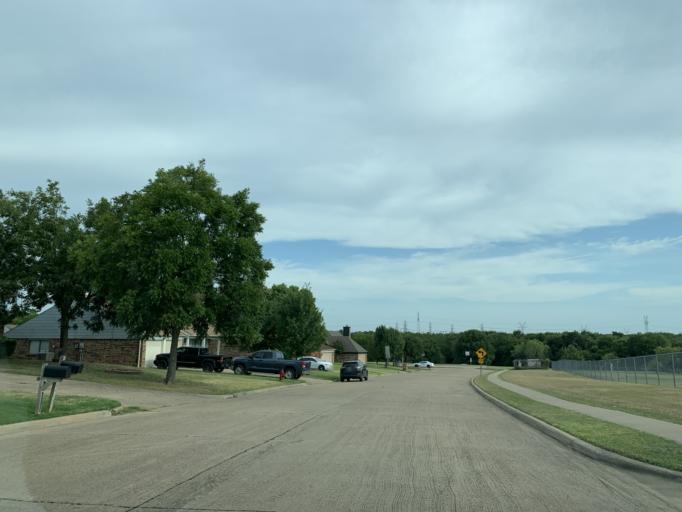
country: US
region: Texas
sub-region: Tarrant County
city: Arlington
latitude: 32.6613
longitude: -97.0455
